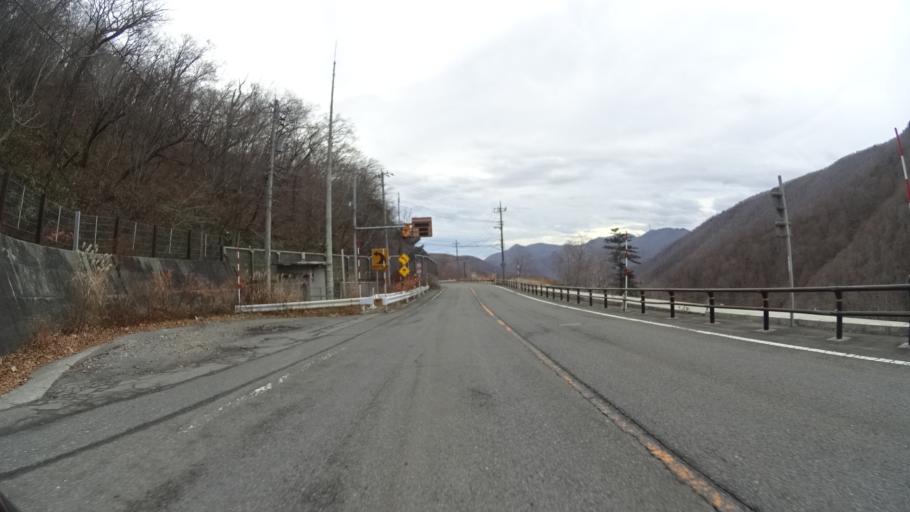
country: JP
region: Gunma
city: Nakanojomachi
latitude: 36.7611
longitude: 138.8278
